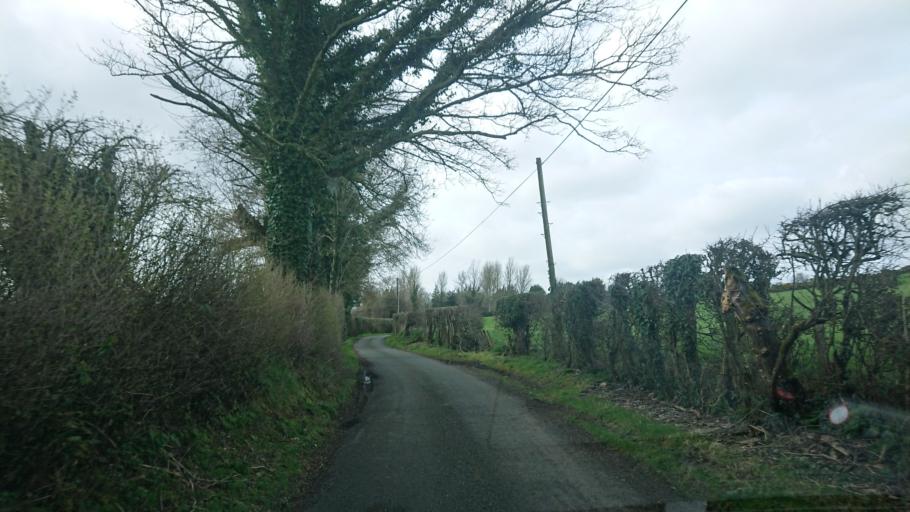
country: IE
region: Leinster
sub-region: Kildare
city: Eadestown
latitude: 53.1627
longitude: -6.6025
